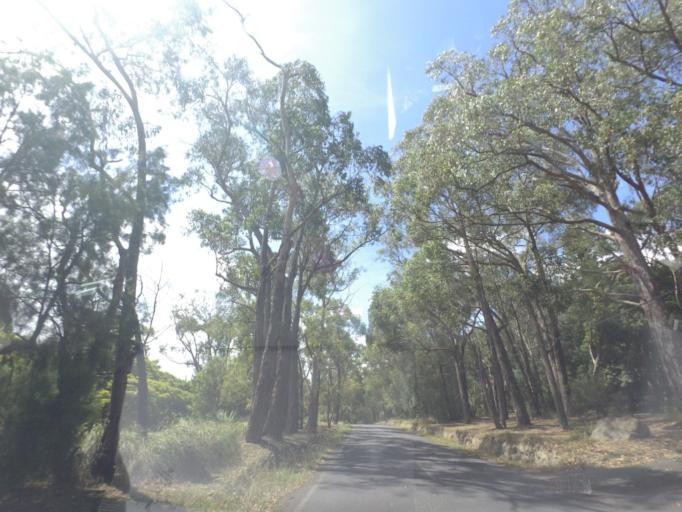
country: AU
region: Victoria
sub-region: Yarra Ranges
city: Montrose
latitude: -37.7928
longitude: 145.3535
